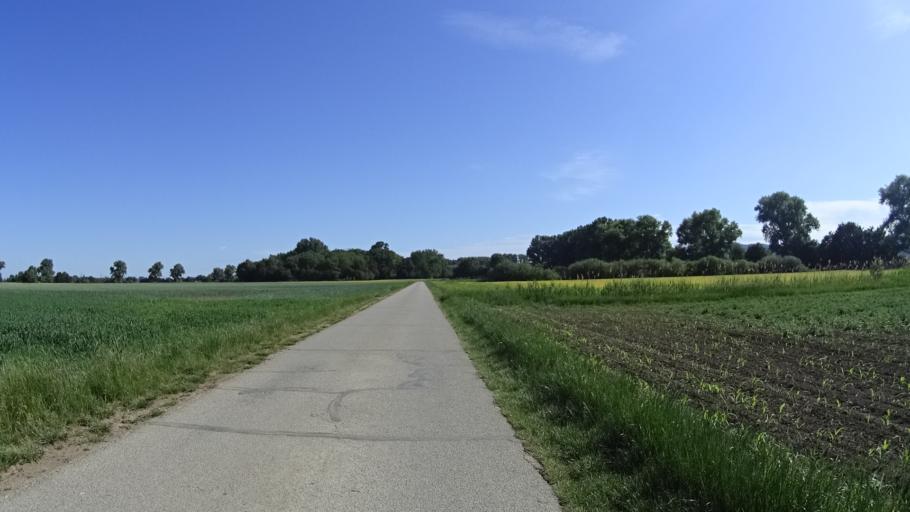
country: DE
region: Hesse
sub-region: Regierungsbezirk Darmstadt
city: Alsbach-Hahnlein
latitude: 49.7470
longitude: 8.5834
